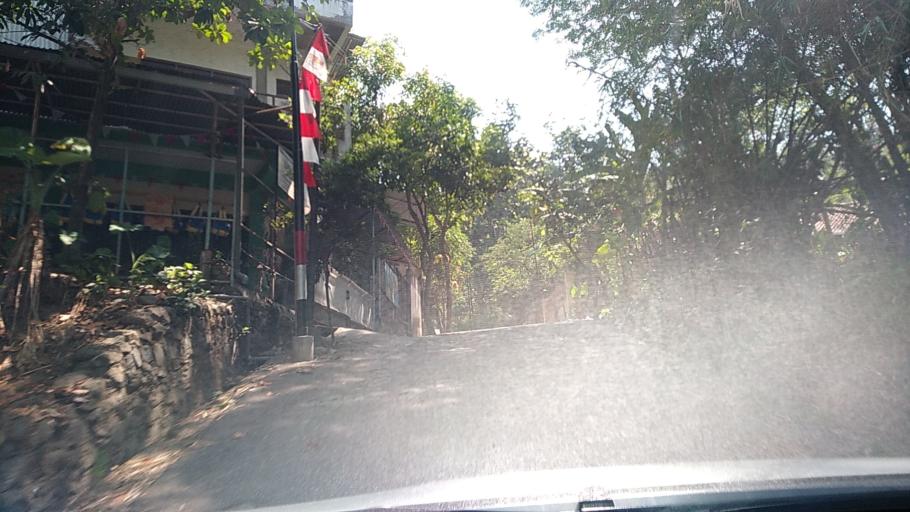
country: ID
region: Central Java
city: Semarang
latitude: -7.0316
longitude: 110.4078
